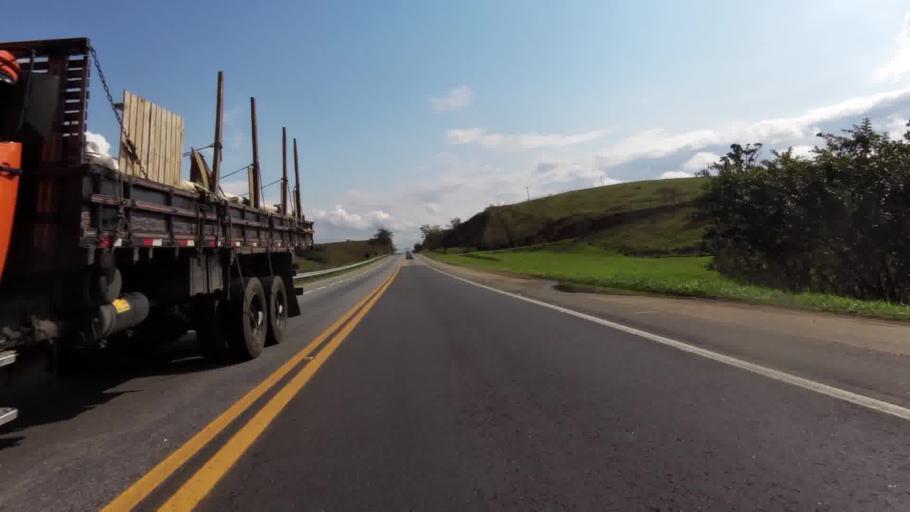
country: BR
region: Rio de Janeiro
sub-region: Macae
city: Macae
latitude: -22.2495
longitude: -41.8168
